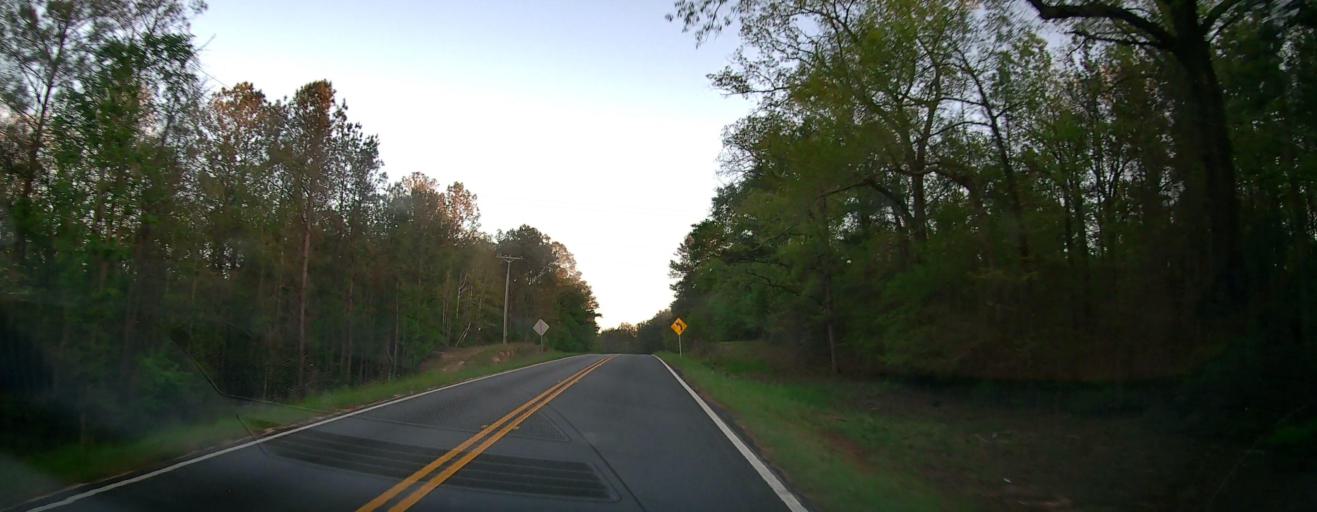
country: US
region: Georgia
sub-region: Marion County
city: Buena Vista
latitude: 32.4304
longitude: -84.5981
